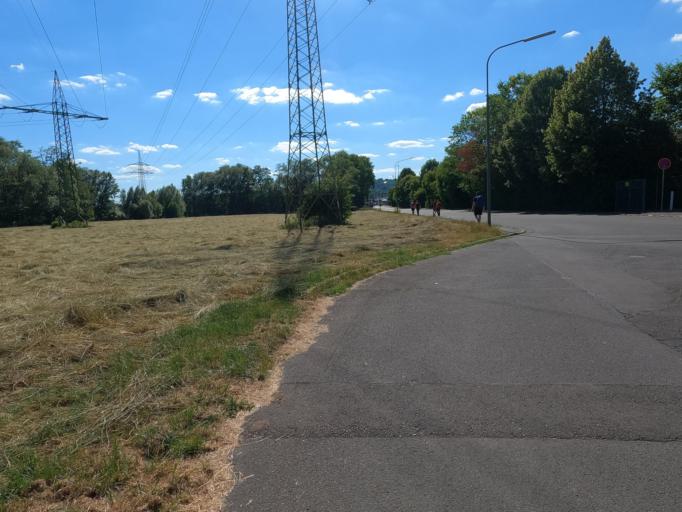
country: DE
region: Hesse
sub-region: Regierungsbezirk Darmstadt
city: Schluchtern
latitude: 50.3560
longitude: 9.5427
